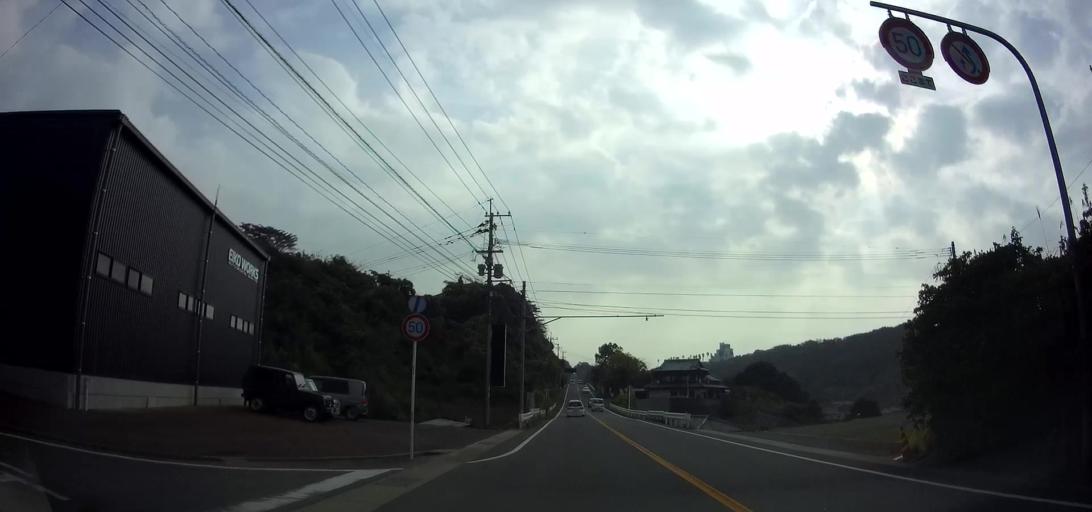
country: JP
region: Nagasaki
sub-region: Isahaya-shi
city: Isahaya
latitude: 32.7988
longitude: 130.0879
